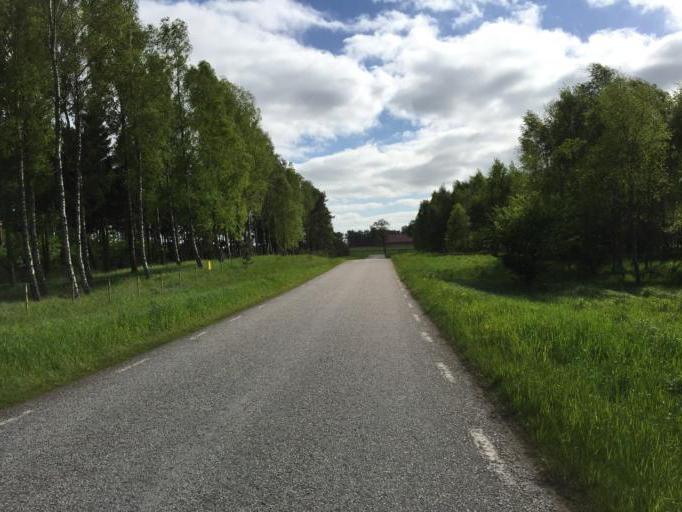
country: SE
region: Skane
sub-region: Sjobo Kommun
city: Blentarp
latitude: 55.6540
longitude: 13.6060
